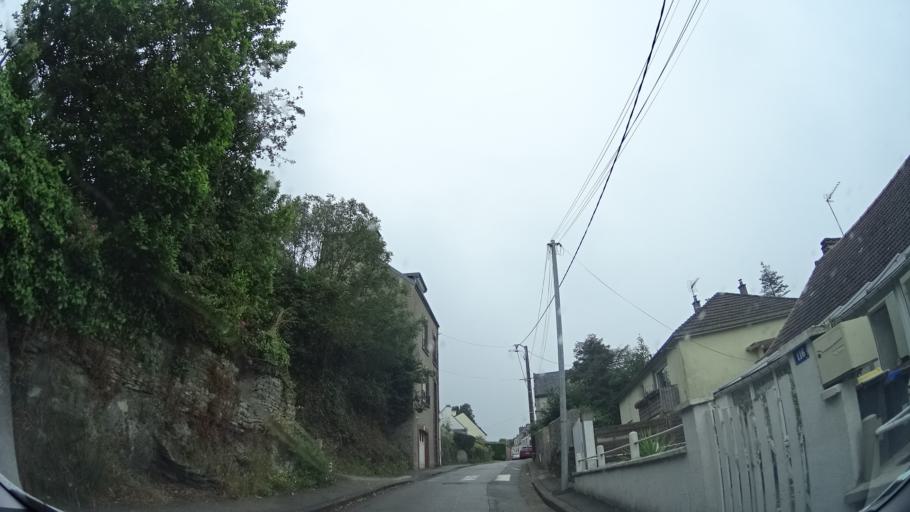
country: FR
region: Lower Normandy
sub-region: Departement de la Manche
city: Octeville
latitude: 49.6315
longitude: -1.6307
